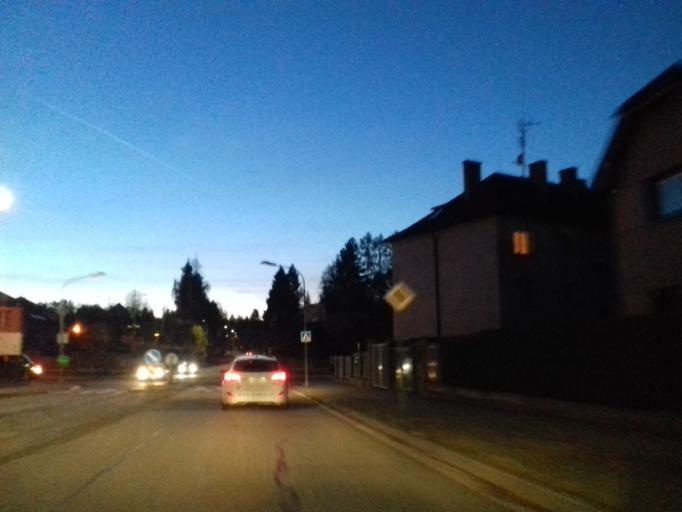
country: CZ
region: Vysocina
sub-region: Okres Pelhrimov
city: Humpolec
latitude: 49.5350
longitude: 15.3593
